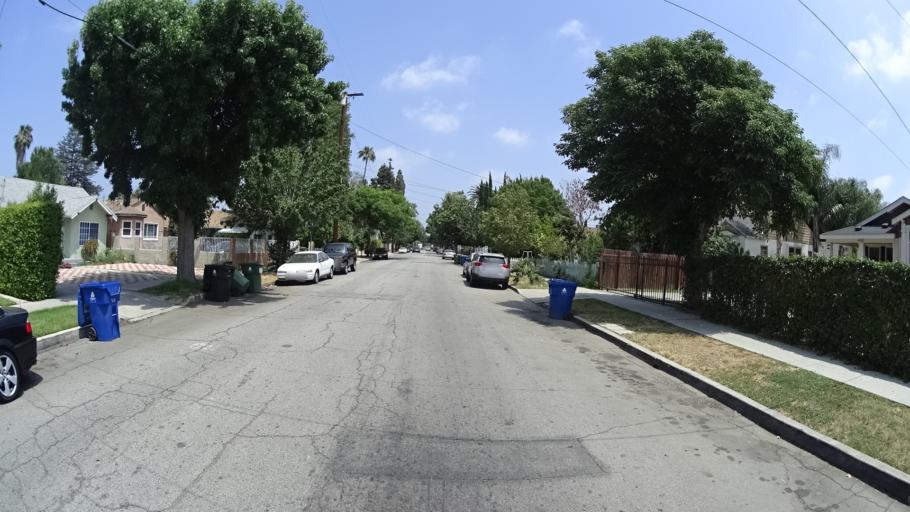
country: US
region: California
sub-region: Los Angeles County
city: Van Nuys
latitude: 34.1922
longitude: -118.4531
